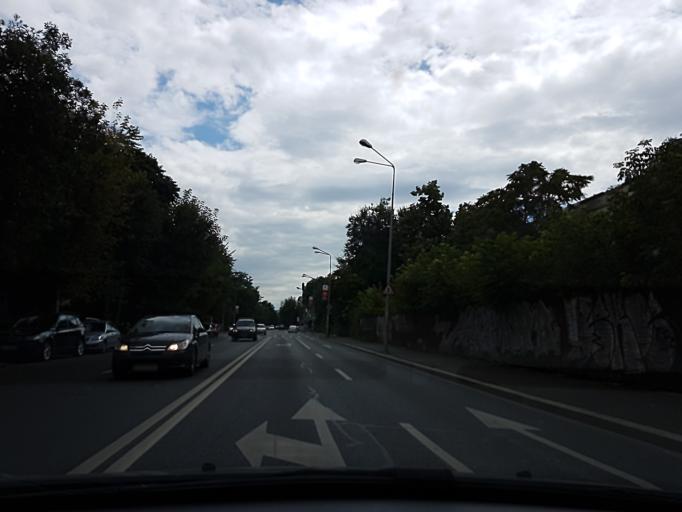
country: RO
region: Bucuresti
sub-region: Municipiul Bucuresti
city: Bucharest
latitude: 44.4644
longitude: 26.1018
